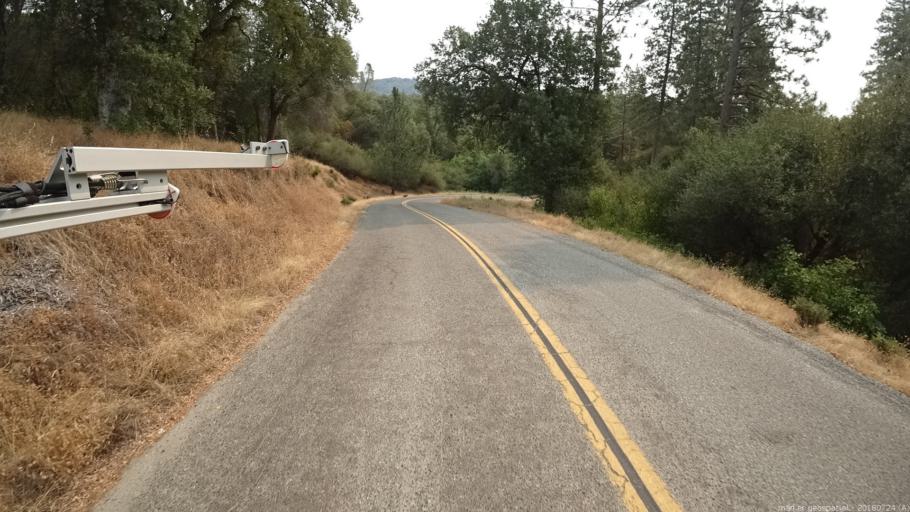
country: US
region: California
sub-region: Madera County
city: Oakhurst
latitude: 37.3356
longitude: -119.6096
